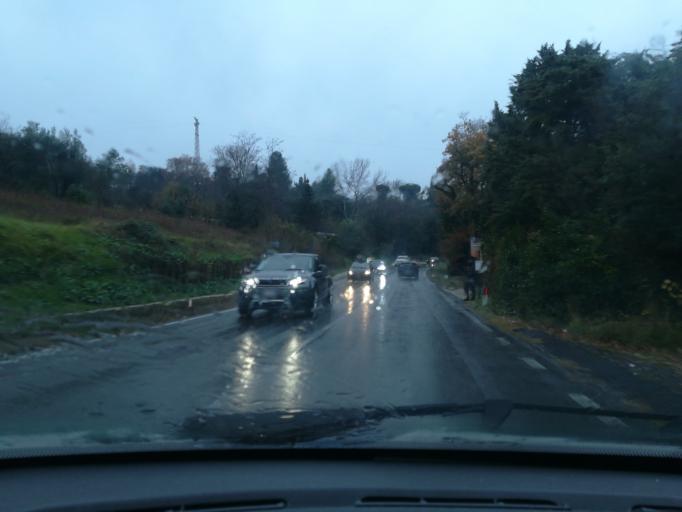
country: IT
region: The Marches
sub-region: Provincia di Macerata
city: Sforzacosta
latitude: 43.2802
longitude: 13.4324
